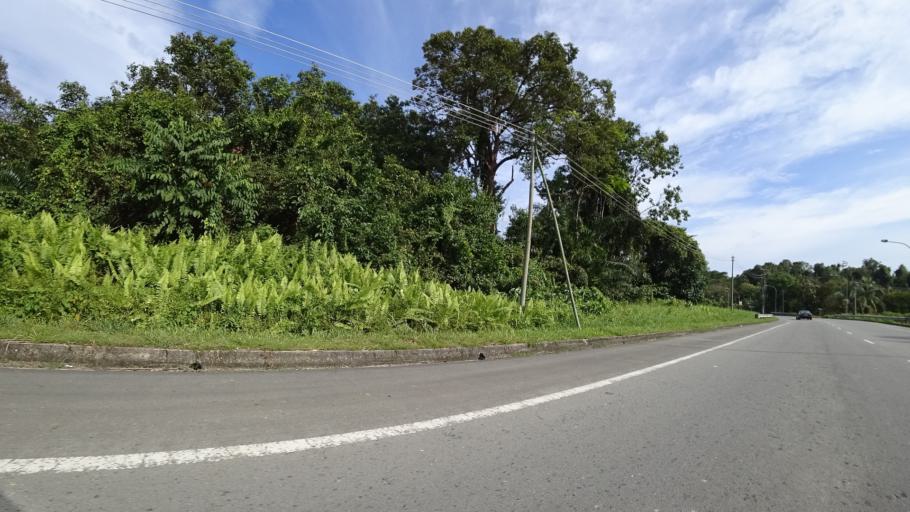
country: BN
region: Brunei and Muara
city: Bandar Seri Begawan
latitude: 4.8716
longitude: 114.8079
